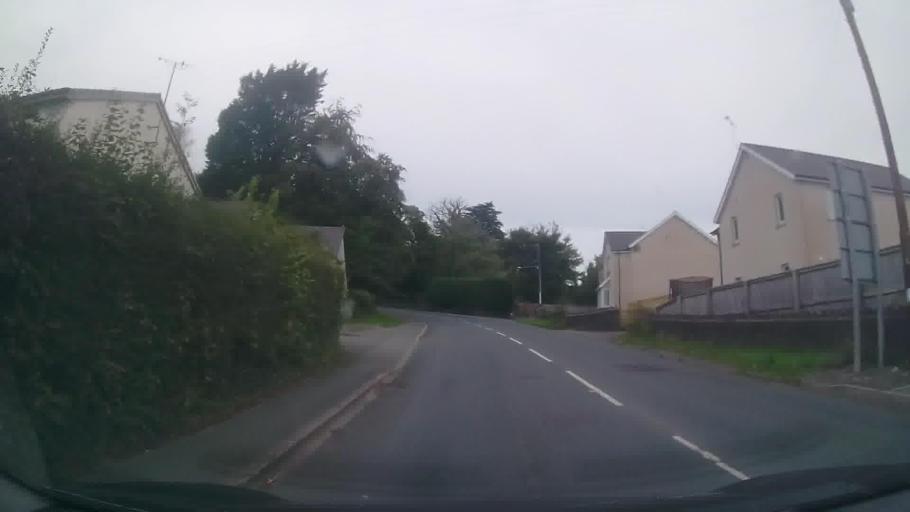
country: GB
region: Wales
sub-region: Pembrokeshire
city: Kilgetty
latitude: 51.7327
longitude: -4.7247
